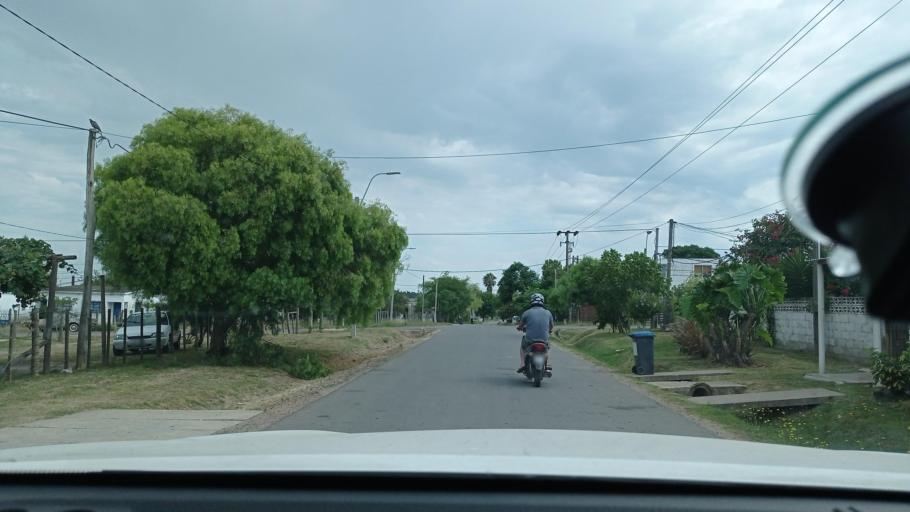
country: UY
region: Canelones
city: Pando
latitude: -34.7149
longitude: -55.9699
